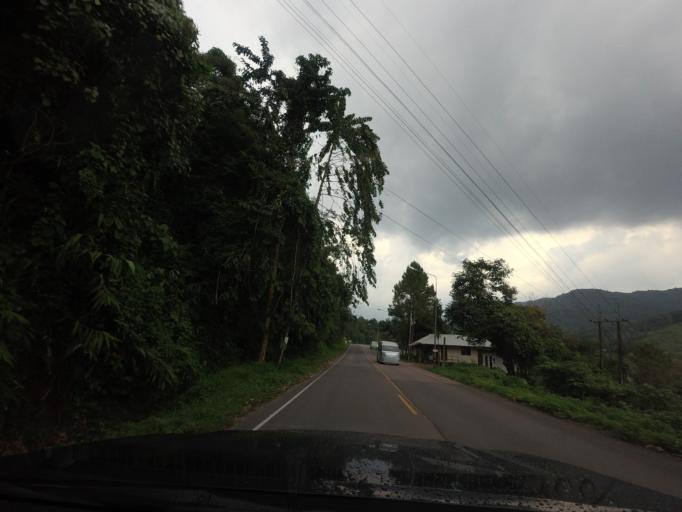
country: TH
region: Nan
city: Bo Kluea
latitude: 19.1507
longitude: 101.1521
